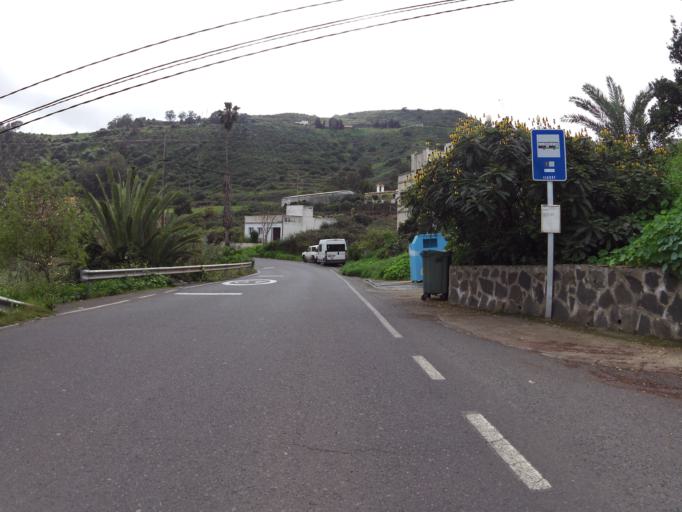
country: ES
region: Canary Islands
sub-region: Provincia de Las Palmas
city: Arucas
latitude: 28.0951
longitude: -15.5326
